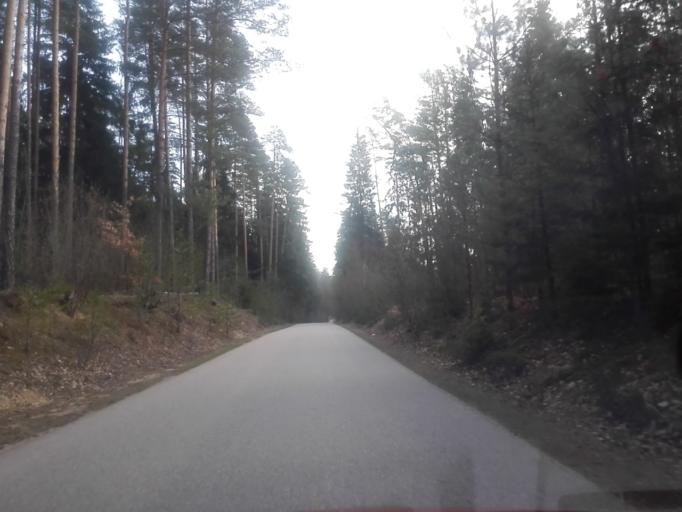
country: PL
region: Podlasie
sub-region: Powiat sejnenski
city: Sejny
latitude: 54.0308
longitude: 23.3749
